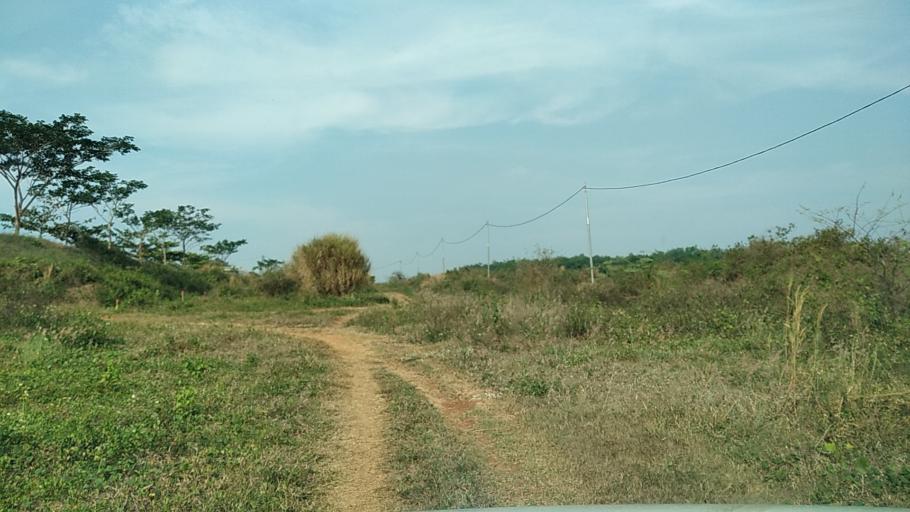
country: ID
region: Central Java
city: Semarang
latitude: -7.0472
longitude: 110.3186
